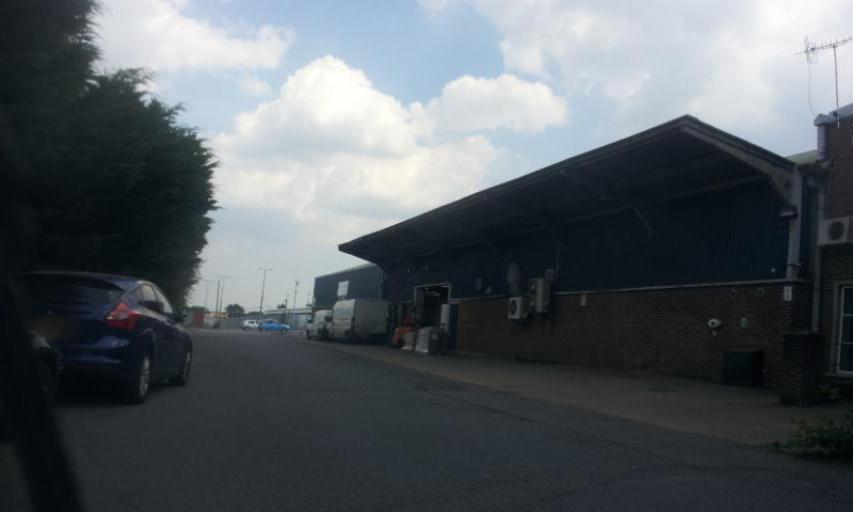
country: GB
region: England
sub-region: Kent
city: Paddock Wood
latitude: 51.1829
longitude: 0.3878
